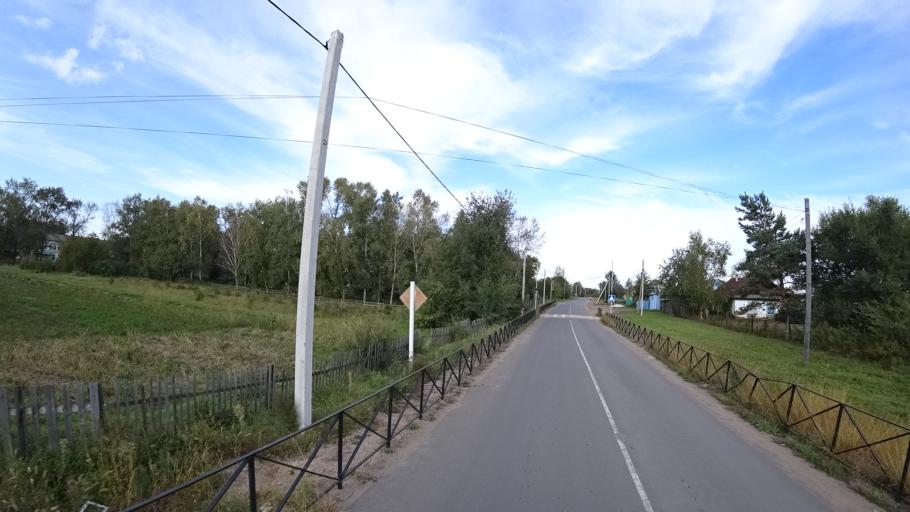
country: RU
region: Amur
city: Arkhara
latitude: 49.3596
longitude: 130.1174
